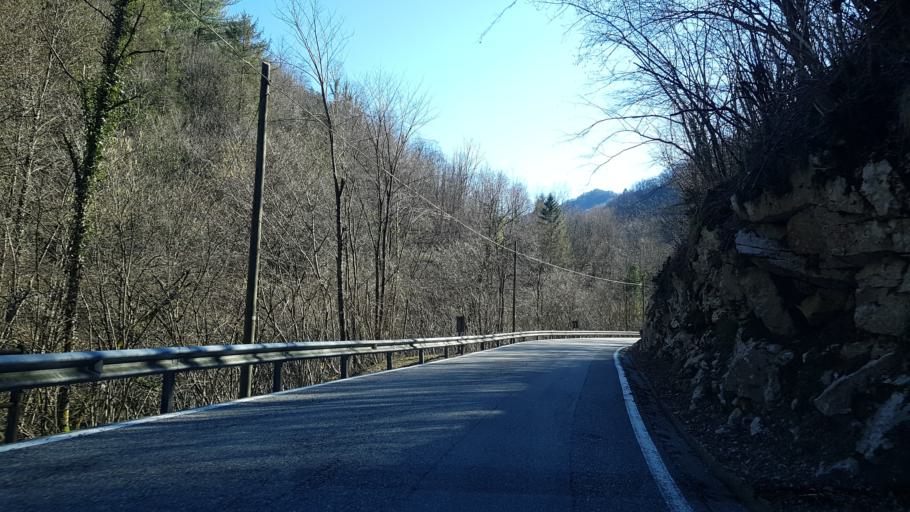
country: IT
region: Friuli Venezia Giulia
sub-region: Provincia di Udine
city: Taipana
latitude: 46.2486
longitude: 13.3258
